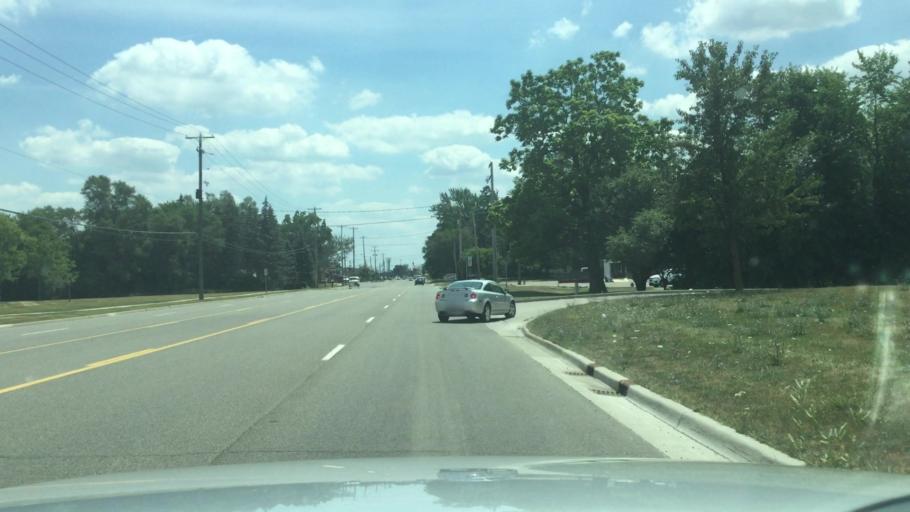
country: US
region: Michigan
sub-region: Genesee County
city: Grand Blanc
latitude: 42.9509
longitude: -83.6575
